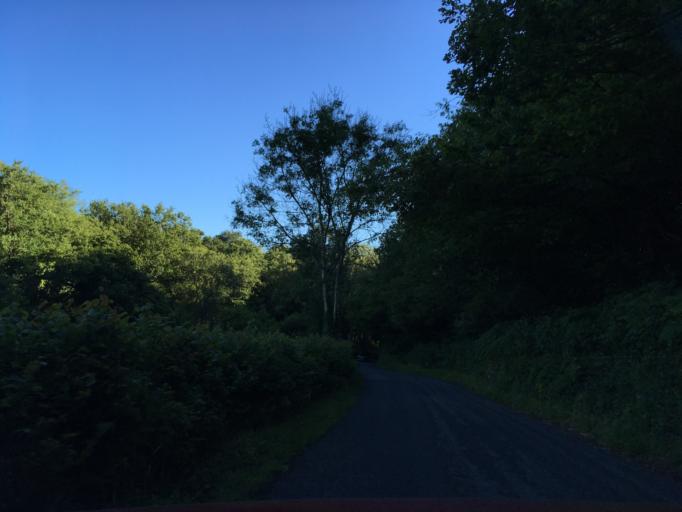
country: GB
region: Wales
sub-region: Monmouthshire
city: Tintern
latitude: 51.6908
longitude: -2.7237
